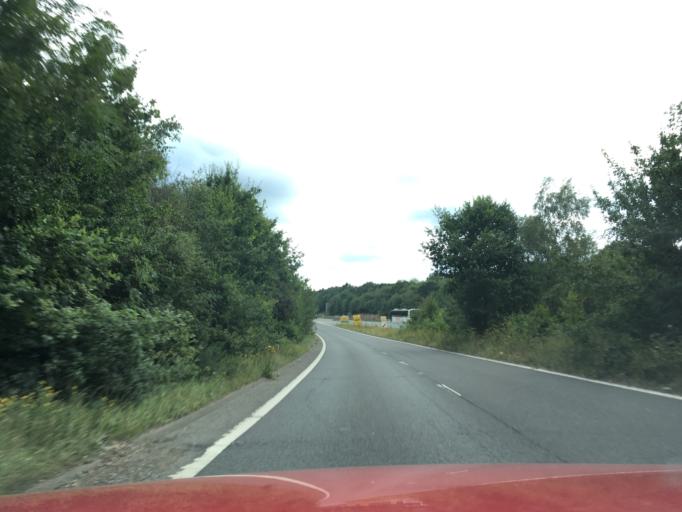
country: GB
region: England
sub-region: West Sussex
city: Copthorne
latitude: 51.1308
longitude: -0.1411
